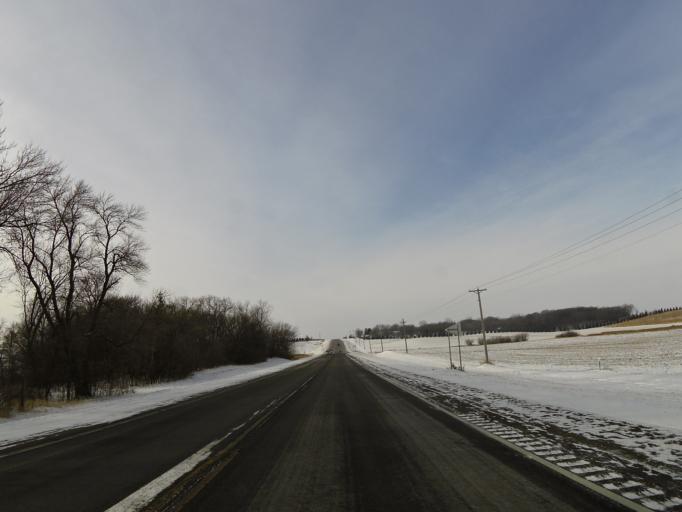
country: US
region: Minnesota
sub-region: McLeod County
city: Lester Prairie
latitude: 44.9062
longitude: -94.0149
